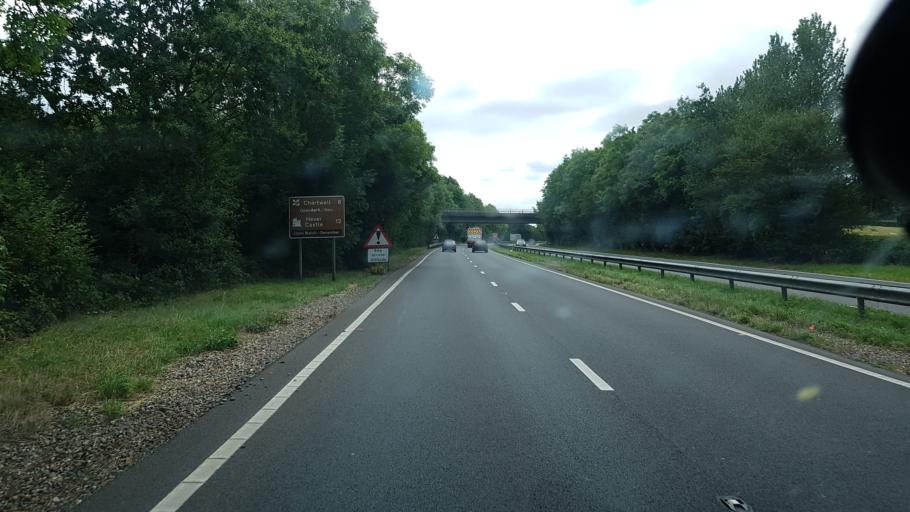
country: GB
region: England
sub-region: Surrey
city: Godstone
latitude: 51.2549
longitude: -0.0575
